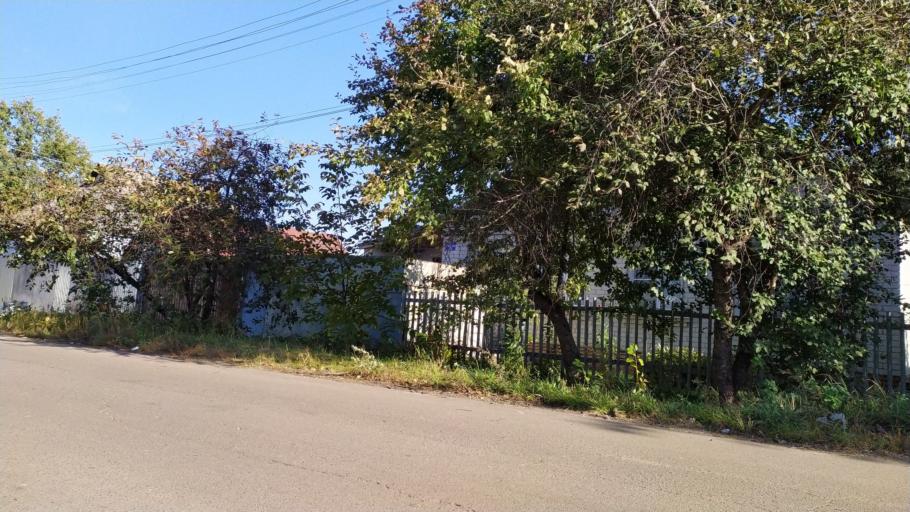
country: RU
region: Kursk
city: Kursk
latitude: 51.6434
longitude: 36.1430
